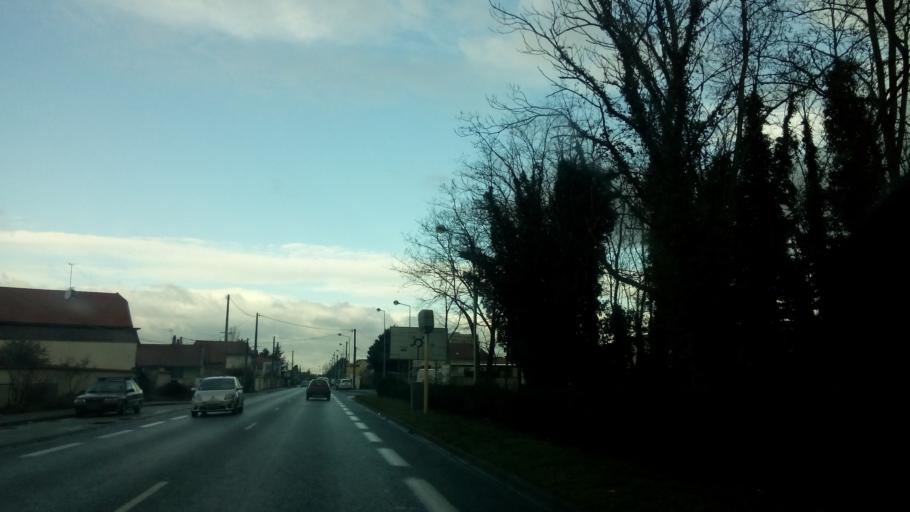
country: FR
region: Rhone-Alpes
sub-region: Departement du Rhone
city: Saint-Priest
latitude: 45.6840
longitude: 4.9511
